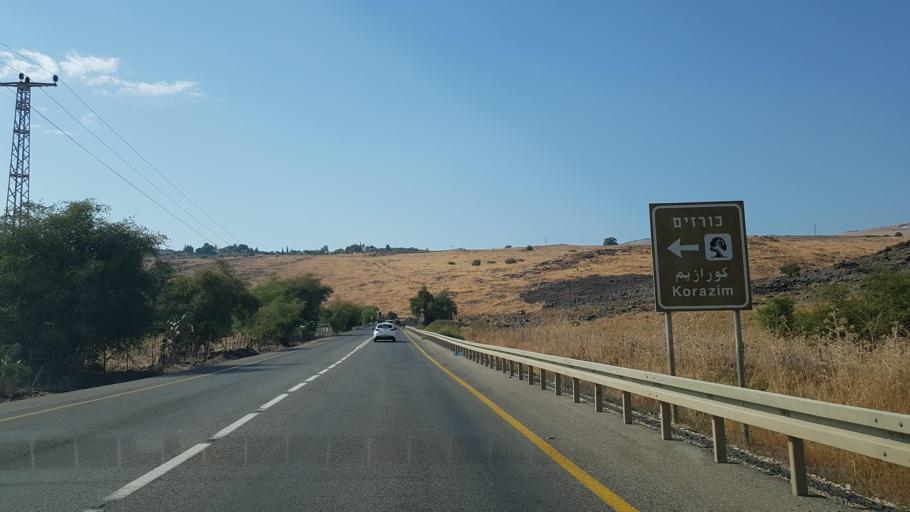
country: IL
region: Northern District
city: Rosh Pinna
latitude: 32.9122
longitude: 35.5678
